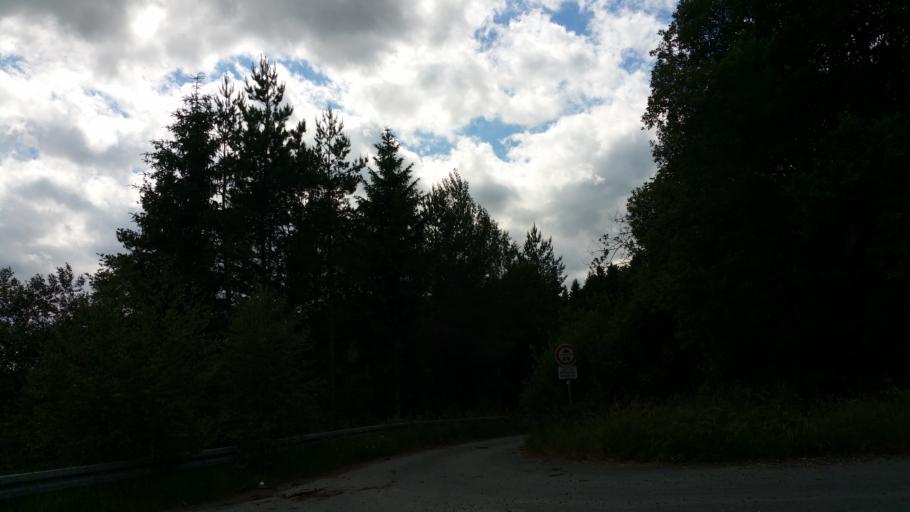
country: DE
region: Bavaria
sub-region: Upper Franconia
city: Schwarzenbach an der Saale
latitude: 50.1959
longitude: 11.9459
